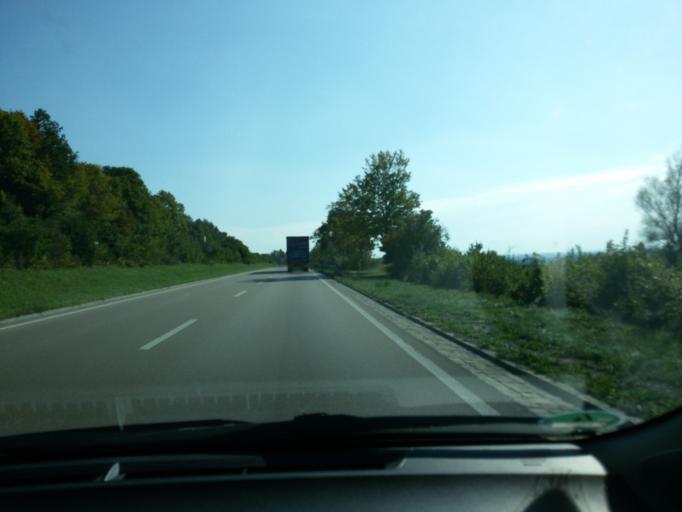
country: DE
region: Bavaria
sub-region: Swabia
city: Donauwoerth
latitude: 48.7259
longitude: 10.7853
